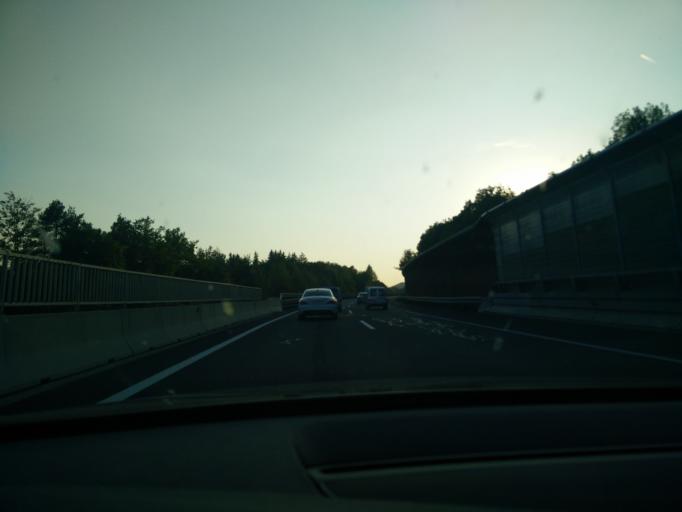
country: AT
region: Carinthia
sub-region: Politischer Bezirk Villach Land
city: Velden am Woerthersee
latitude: 46.6225
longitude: 14.0451
